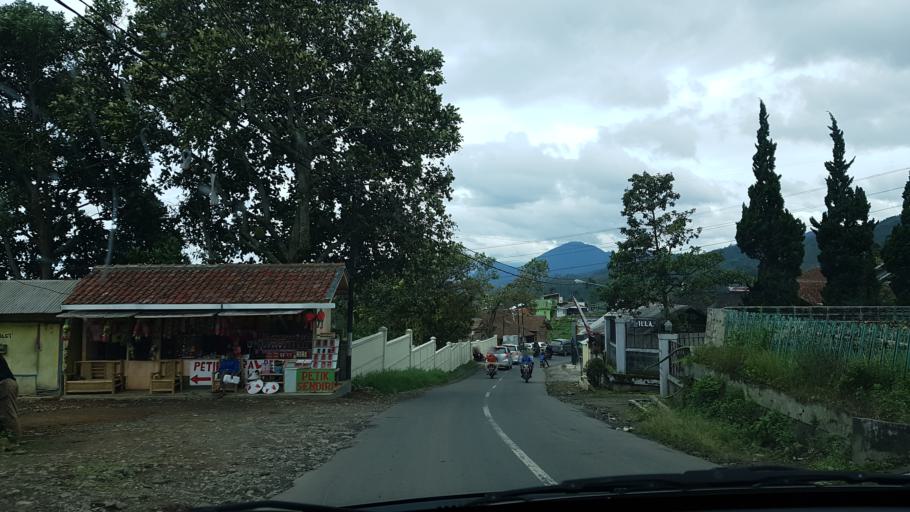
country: ID
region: West Java
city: Banjar
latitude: -7.1214
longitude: 107.4260
